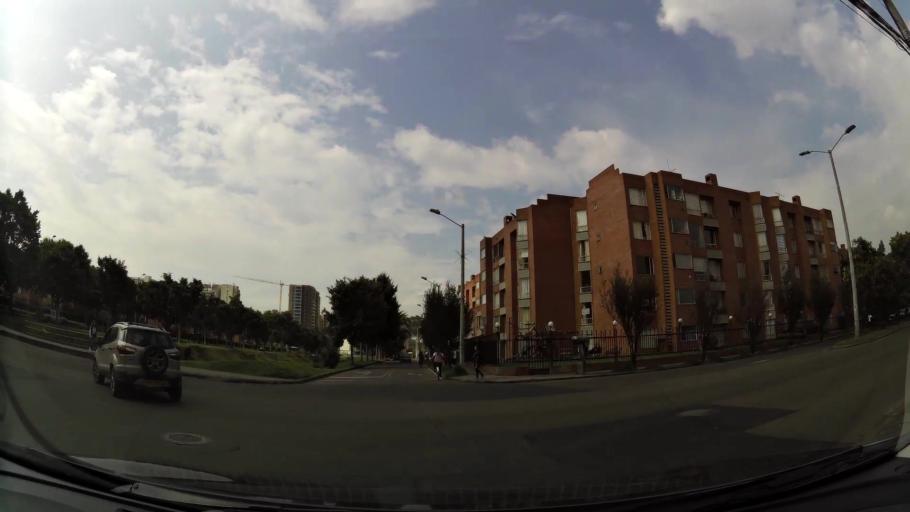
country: CO
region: Bogota D.C.
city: Barrio San Luis
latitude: 4.7356
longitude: -74.0552
